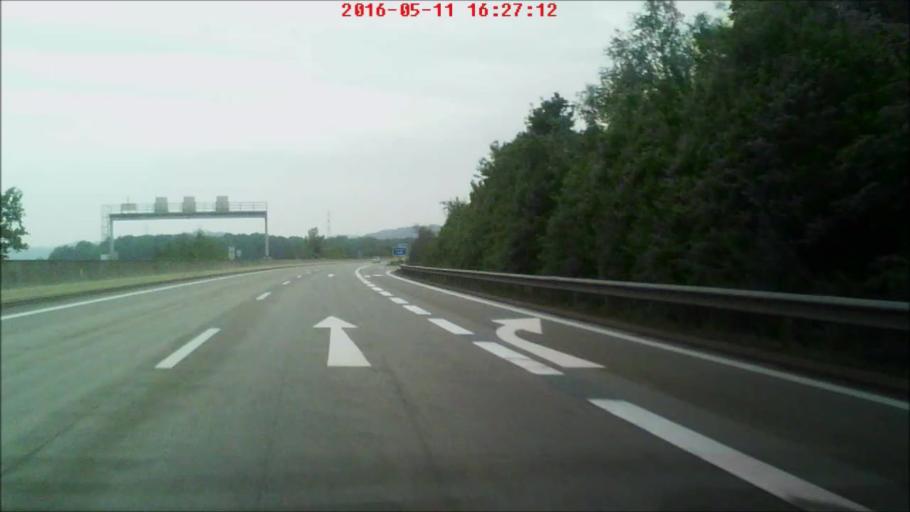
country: AT
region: Styria
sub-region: Politischer Bezirk Leibnitz
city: Strass in Steiermark
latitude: 46.7287
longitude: 15.6453
